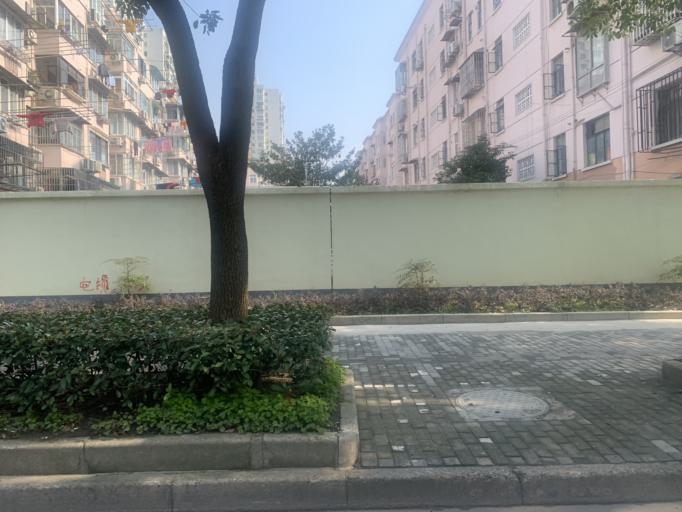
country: CN
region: Shanghai Shi
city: Huamu
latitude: 31.1849
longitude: 121.5148
